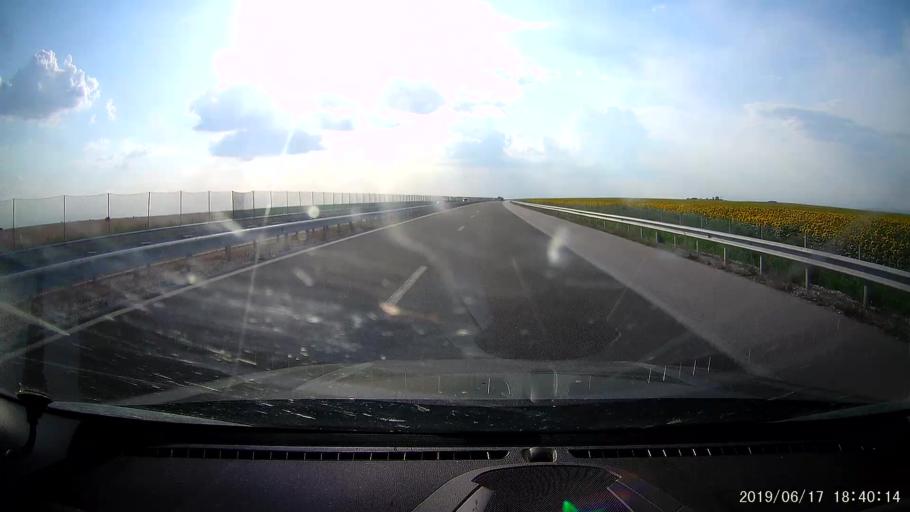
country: BG
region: Stara Zagora
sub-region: Obshtina Chirpan
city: Chirpan
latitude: 42.1531
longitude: 25.2834
